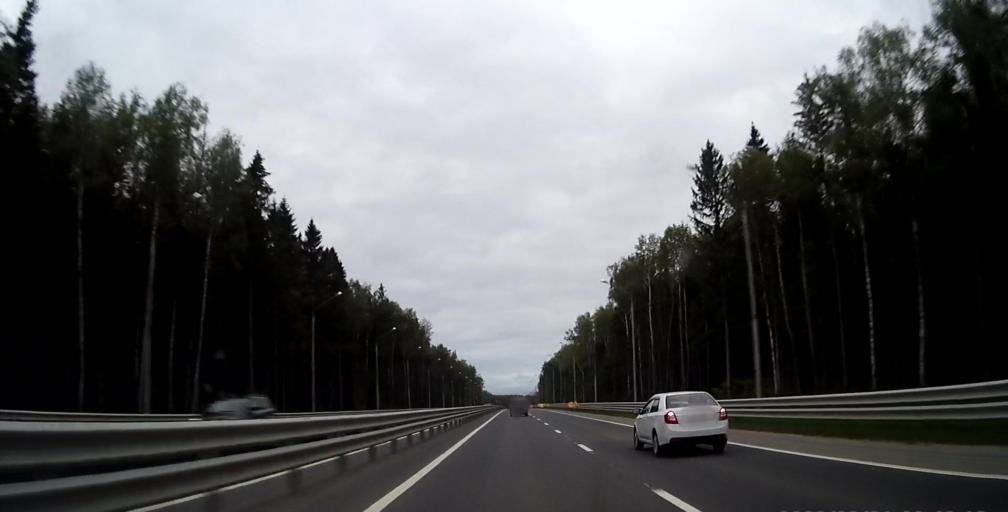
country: RU
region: Moskovskaya
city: Klimovsk
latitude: 55.3839
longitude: 37.5195
